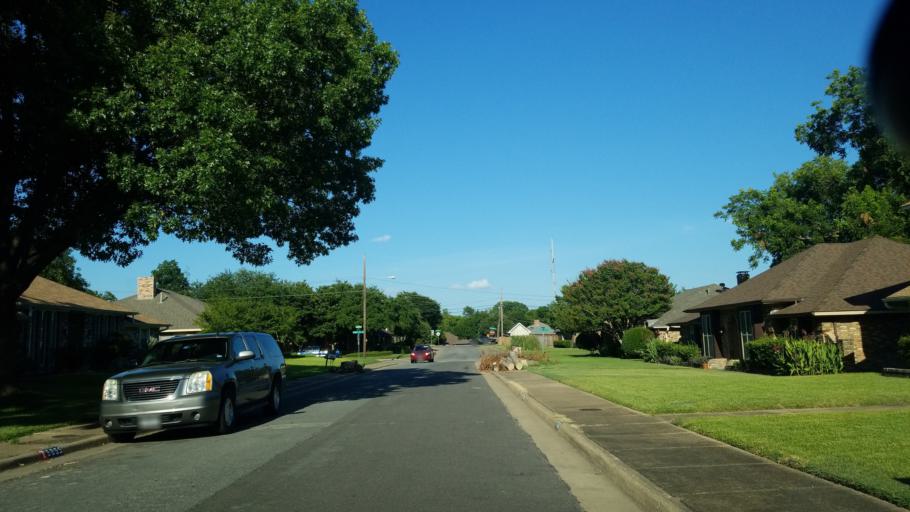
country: US
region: Texas
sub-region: Dallas County
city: Balch Springs
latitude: 32.7837
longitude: -96.7017
